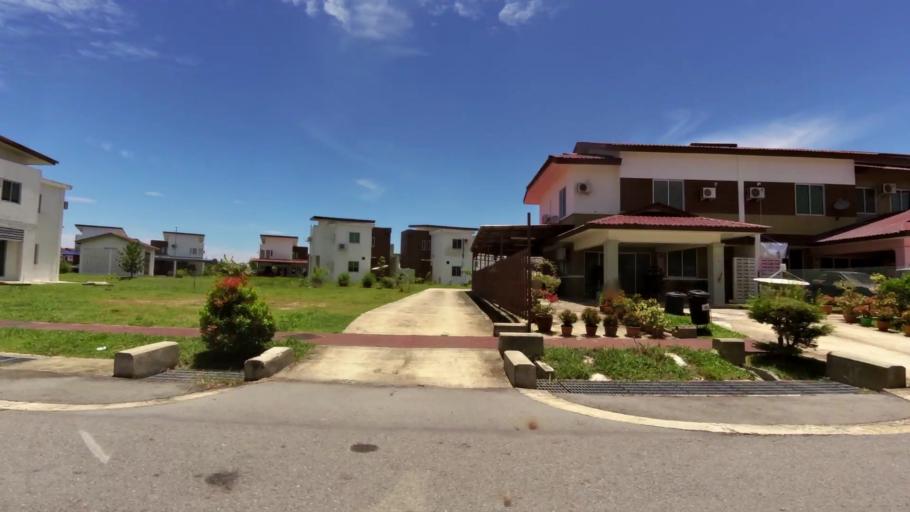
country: BN
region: Brunei and Muara
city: Bandar Seri Begawan
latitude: 5.0051
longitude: 115.0065
